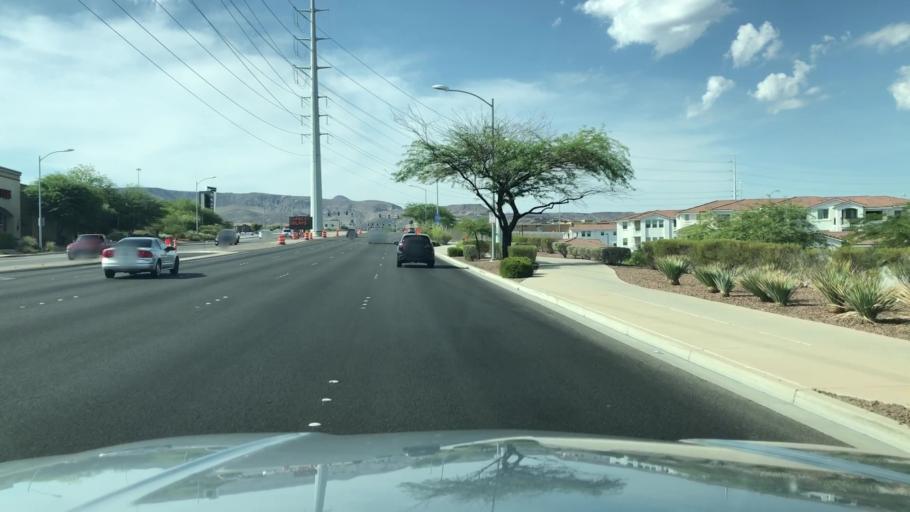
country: US
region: Nevada
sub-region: Clark County
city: Whitney
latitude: 36.0332
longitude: -115.0472
